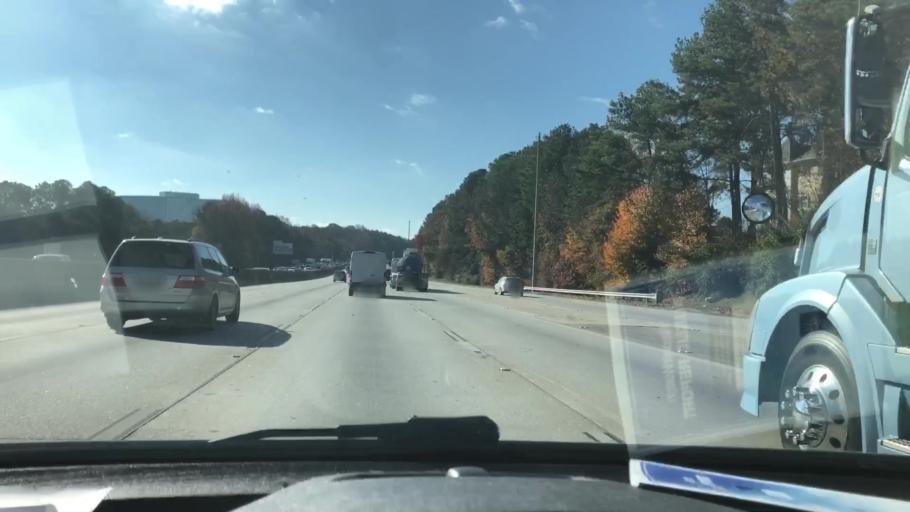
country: US
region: Georgia
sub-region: DeKalb County
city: Clarkston
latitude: 33.8412
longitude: -84.2500
